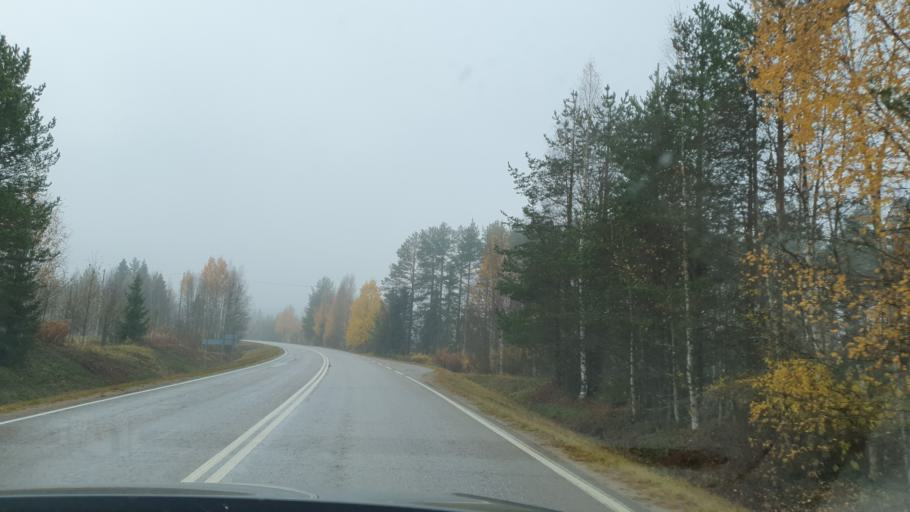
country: FI
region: Lapland
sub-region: Rovaniemi
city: Rovaniemi
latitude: 66.8193
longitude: 25.3951
